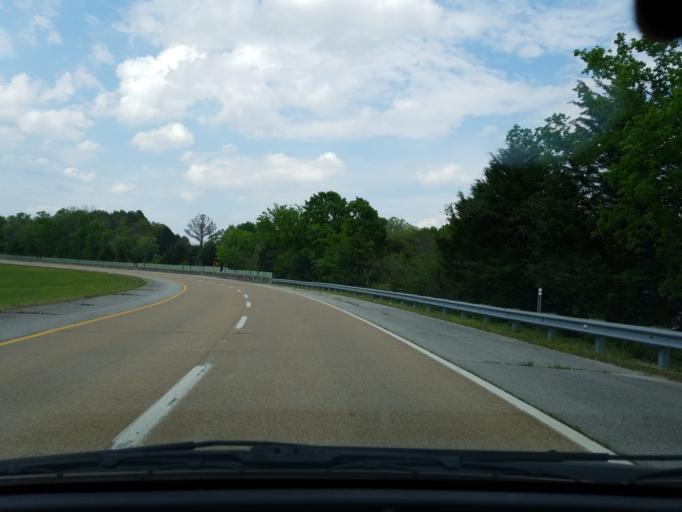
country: US
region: Tennessee
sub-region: Hamilton County
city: Red Bank
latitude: 35.1146
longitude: -85.2484
